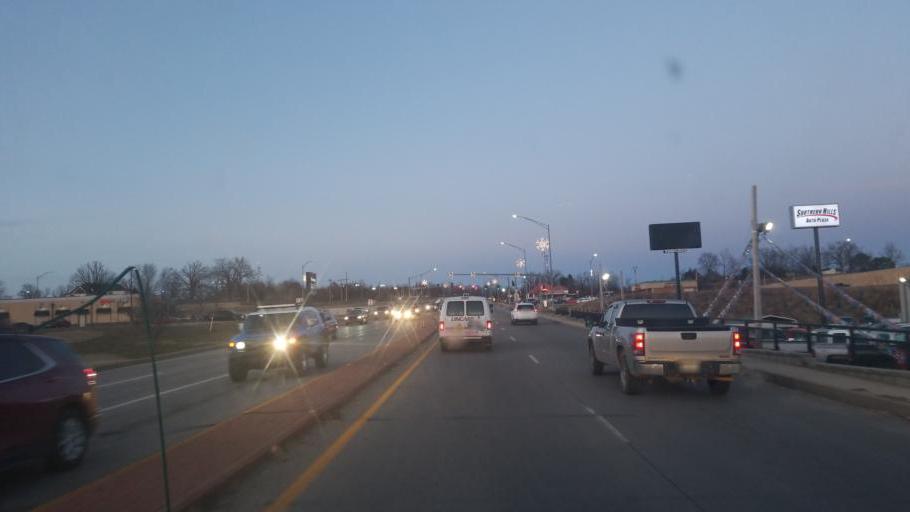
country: US
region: Missouri
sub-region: Howell County
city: West Plains
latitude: 36.7164
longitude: -91.8734
